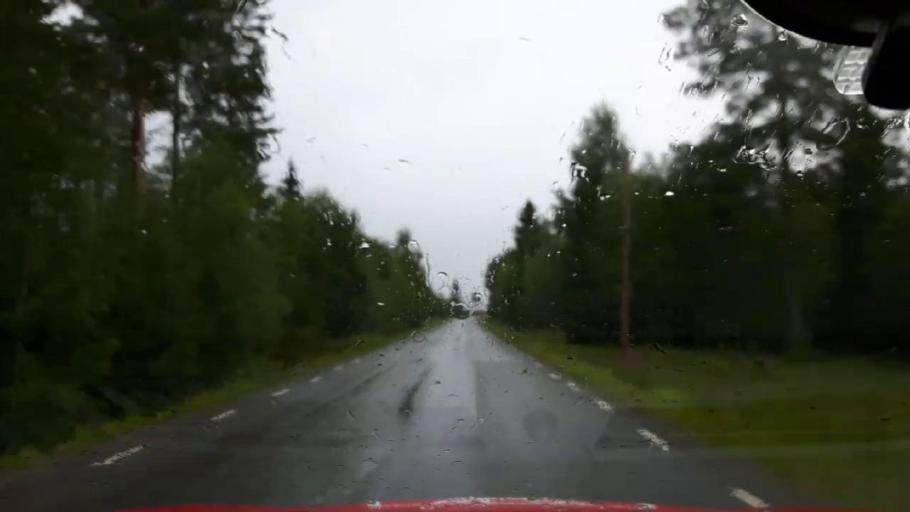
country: SE
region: Jaemtland
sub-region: OEstersunds Kommun
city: Brunflo
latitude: 62.9898
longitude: 14.8011
